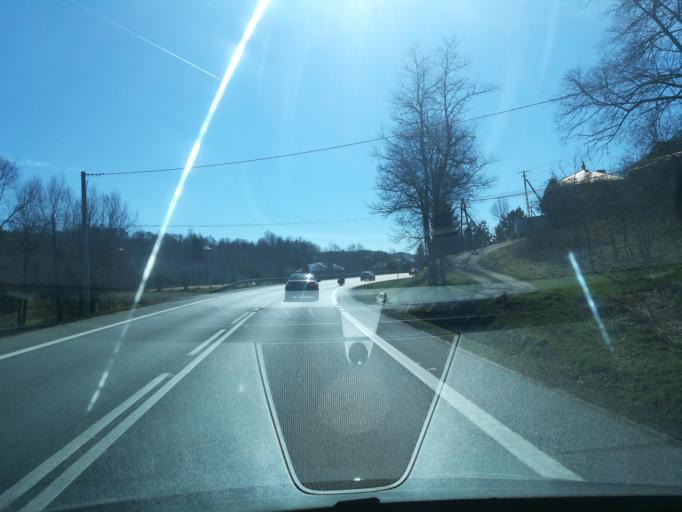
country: PL
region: Subcarpathian Voivodeship
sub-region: Powiat strzyzowski
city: Niebylec
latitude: 49.8723
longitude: 21.9058
